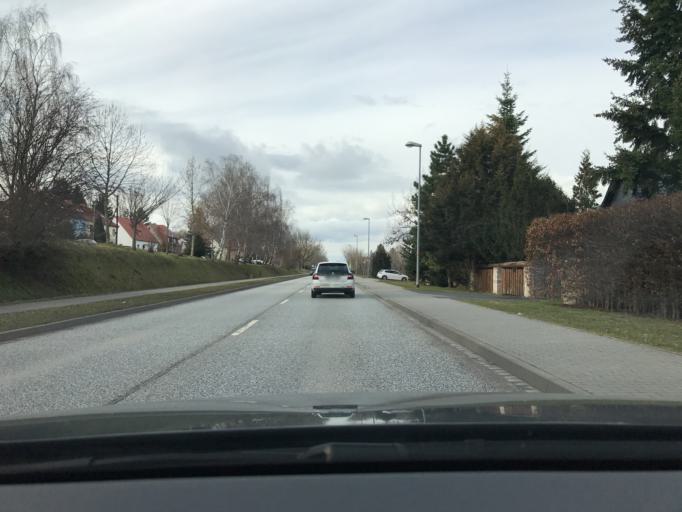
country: DE
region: Saxony-Anhalt
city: Volkstedt
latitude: 51.5155
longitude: 11.5654
